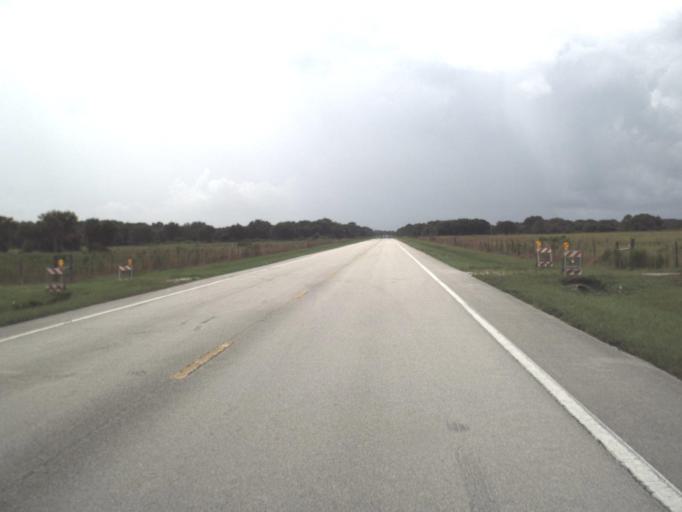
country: US
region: Florida
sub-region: Sarasota County
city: Warm Mineral Springs
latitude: 27.1935
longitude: -82.1711
